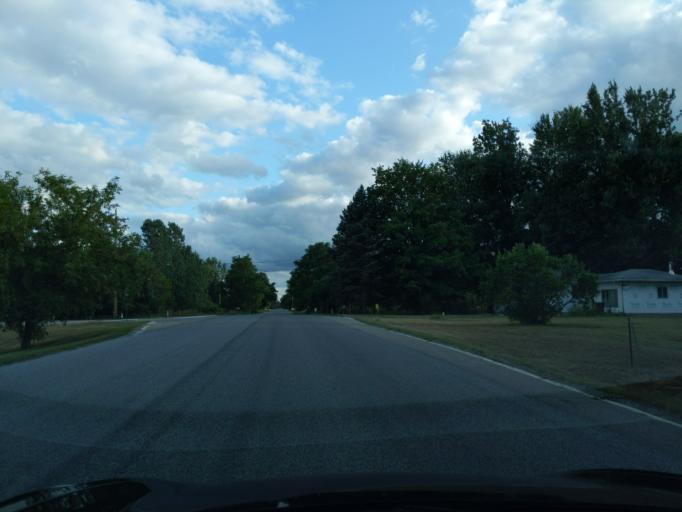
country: US
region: Michigan
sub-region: Ingham County
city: Holt
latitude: 42.6313
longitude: -84.5824
